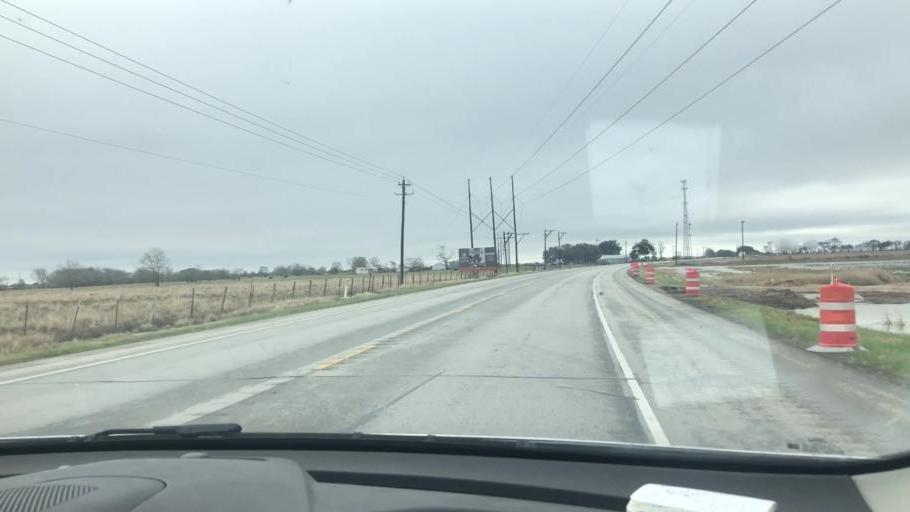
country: US
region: Texas
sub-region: Wharton County
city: Boling
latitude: 29.1443
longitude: -95.9866
